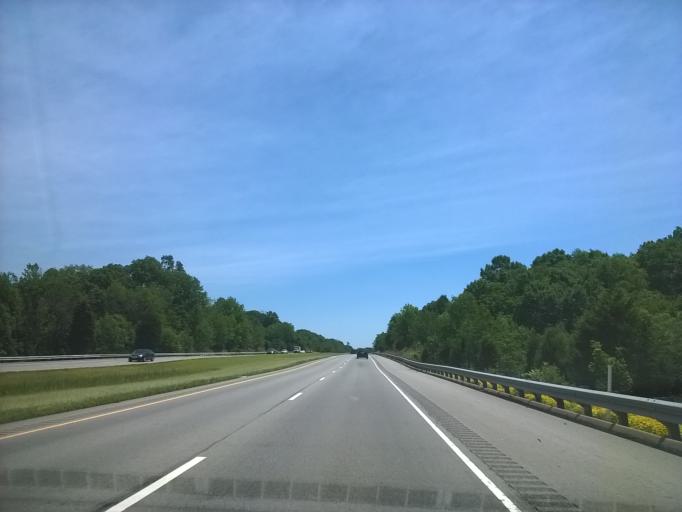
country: US
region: Indiana
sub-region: Dearborn County
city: Bright
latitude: 39.2738
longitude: -84.9239
